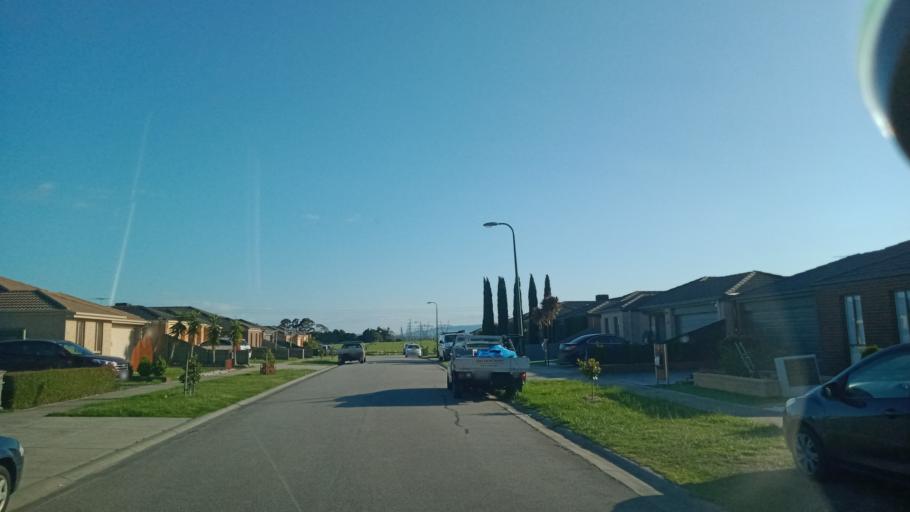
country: AU
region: Victoria
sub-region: Casey
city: Cranbourne West
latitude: -38.0887
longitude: 145.2588
